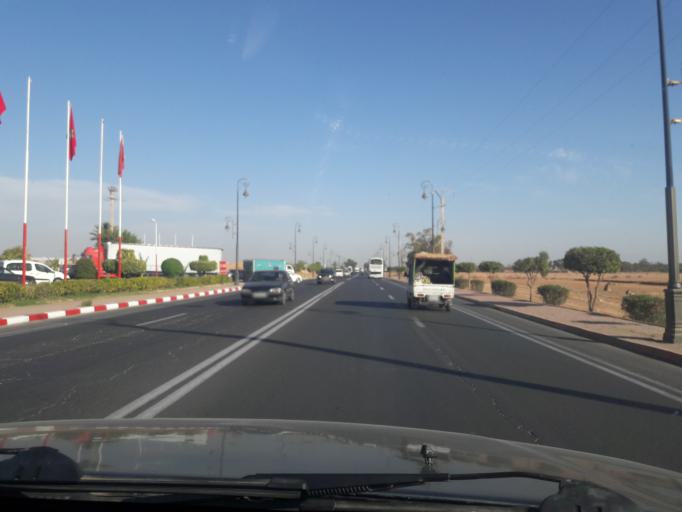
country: MA
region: Marrakech-Tensift-Al Haouz
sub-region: Marrakech
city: Marrakesh
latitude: 31.6481
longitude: -7.9409
